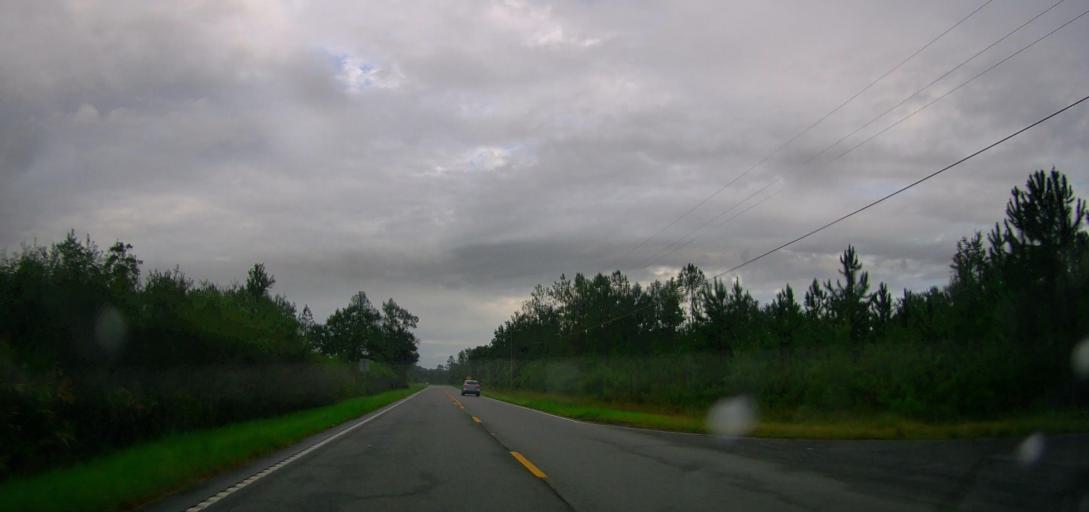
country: US
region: Georgia
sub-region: Ware County
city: Deenwood
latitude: 31.2814
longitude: -82.4281
